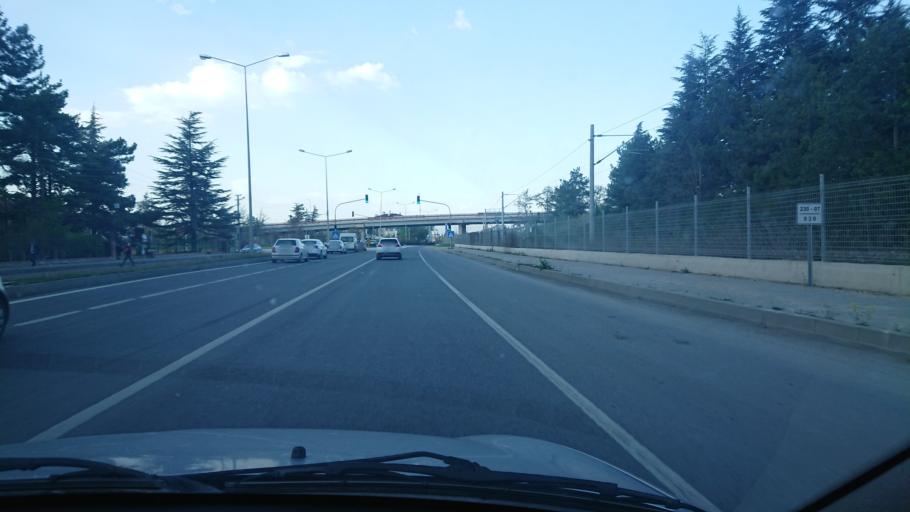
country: TR
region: Eskisehir
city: Eskisehir
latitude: 39.7671
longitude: 30.4800
